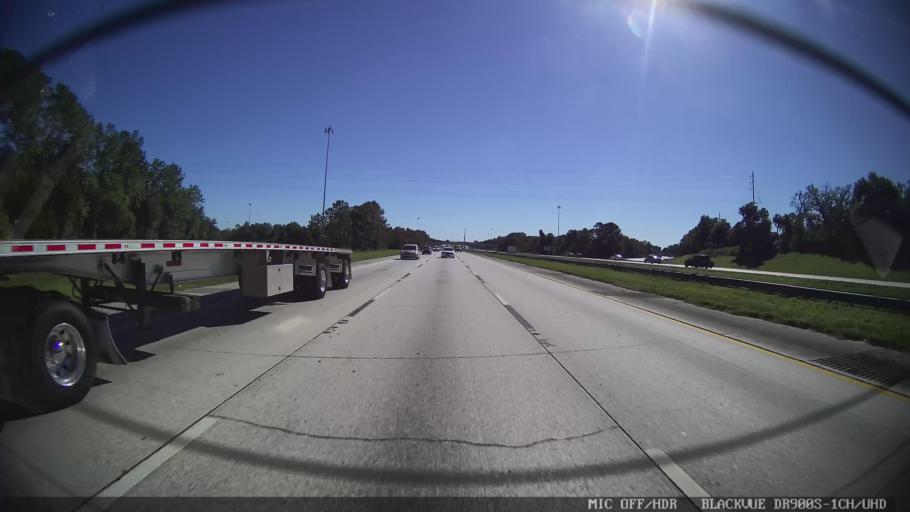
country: US
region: Florida
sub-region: Hillsborough County
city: Mango
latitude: 27.9919
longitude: -82.3254
